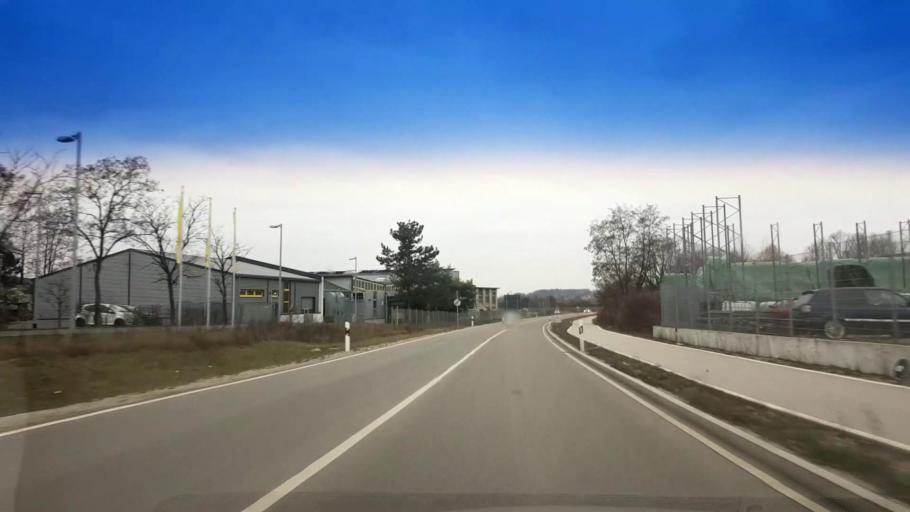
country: DE
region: Bavaria
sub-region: Upper Franconia
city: Pettstadt
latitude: 49.8034
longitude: 10.9496
